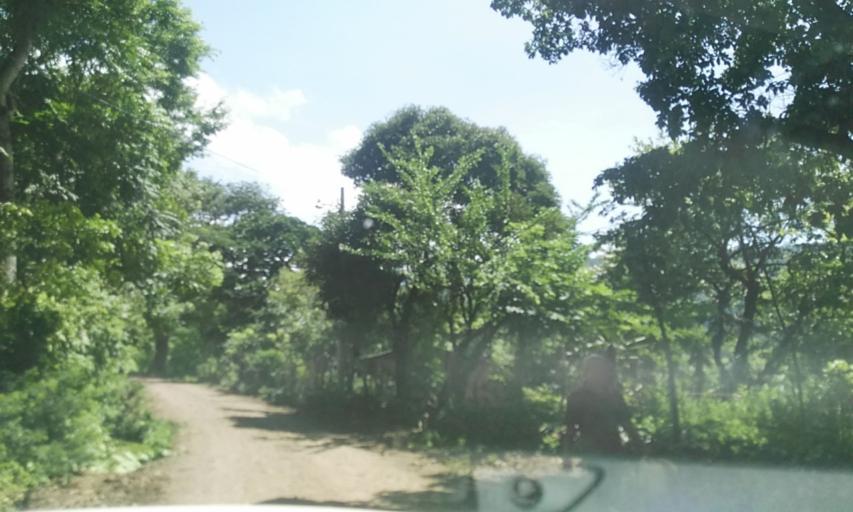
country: NI
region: Matagalpa
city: Terrabona
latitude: 12.7366
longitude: -85.9263
